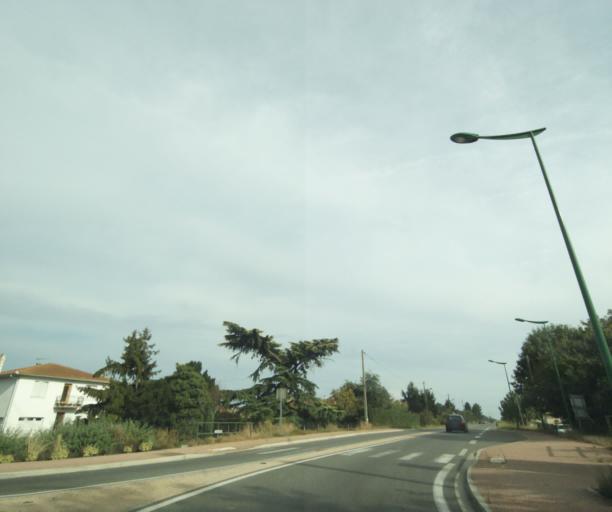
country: FR
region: Midi-Pyrenees
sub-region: Departement du Tarn-et-Garonne
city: Verdun-sur-Garonne
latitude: 43.8799
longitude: 1.2567
